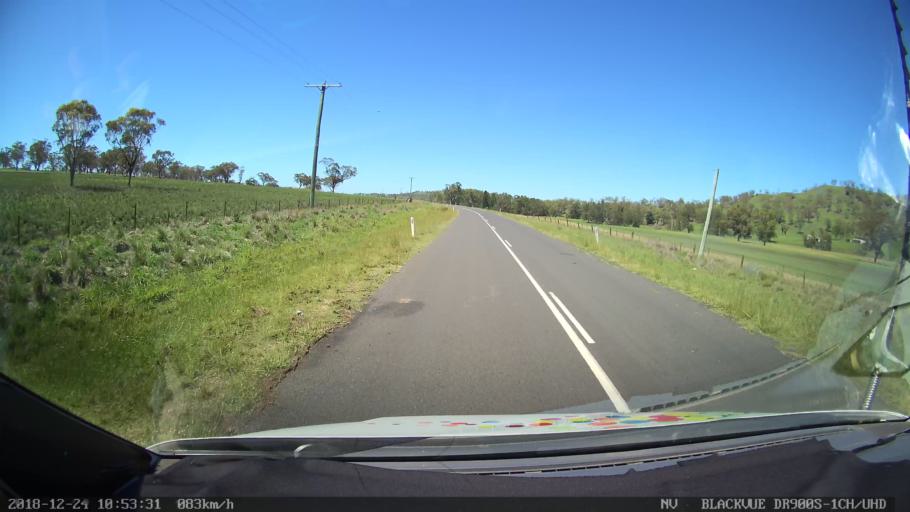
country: AU
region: New South Wales
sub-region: Upper Hunter Shire
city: Merriwa
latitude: -31.9926
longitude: 150.4205
